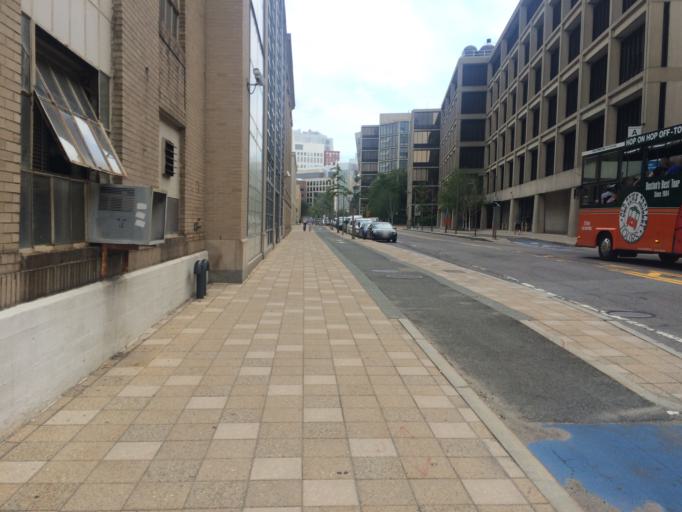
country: US
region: Massachusetts
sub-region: Middlesex County
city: Cambridge
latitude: 42.3607
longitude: -71.0940
